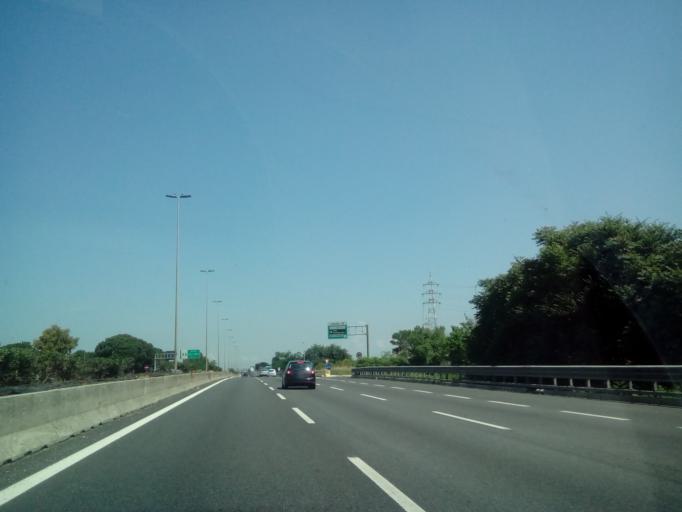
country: IT
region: Latium
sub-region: Citta metropolitana di Roma Capitale
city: Setteville
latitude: 41.9076
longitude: 12.6157
